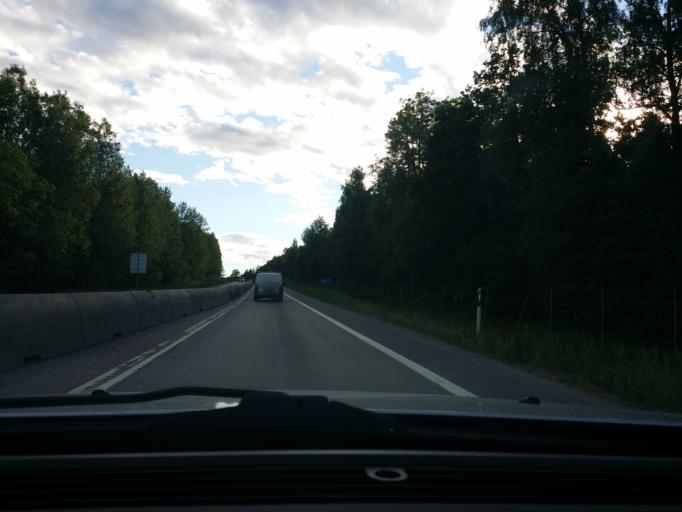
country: SE
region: Stockholm
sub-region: Jarfalla Kommun
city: Jakobsberg
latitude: 59.4776
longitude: 17.8353
